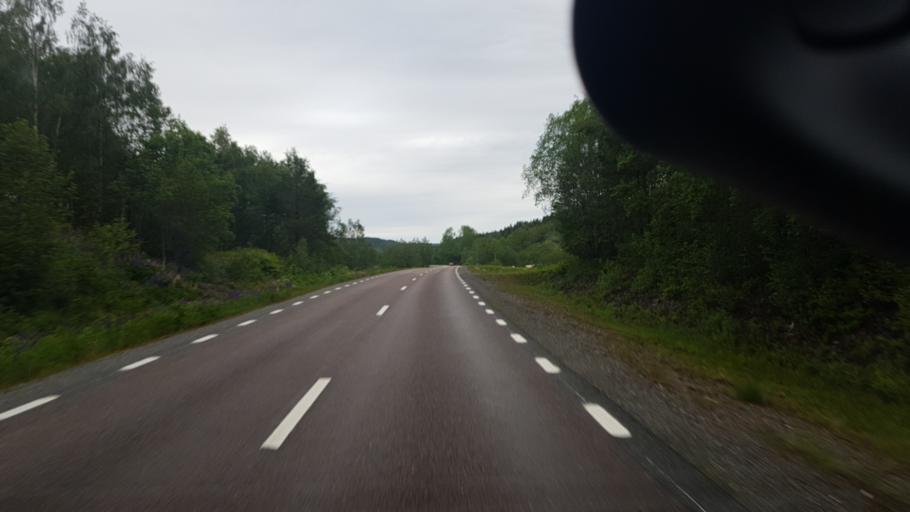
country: SE
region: Vaermland
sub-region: Arjangs Kommun
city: Arjaeng
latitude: 59.6268
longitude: 12.1404
